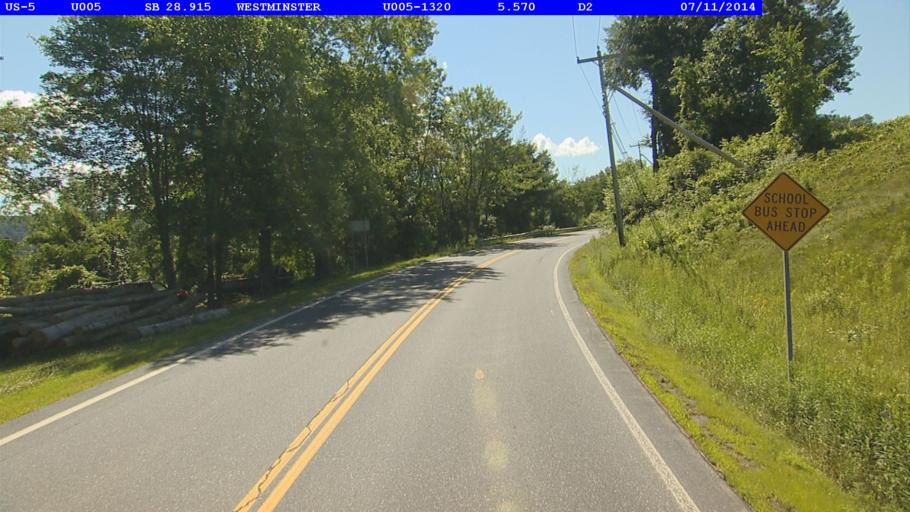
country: US
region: Vermont
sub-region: Windham County
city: Bellows Falls
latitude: 43.0914
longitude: -72.4402
